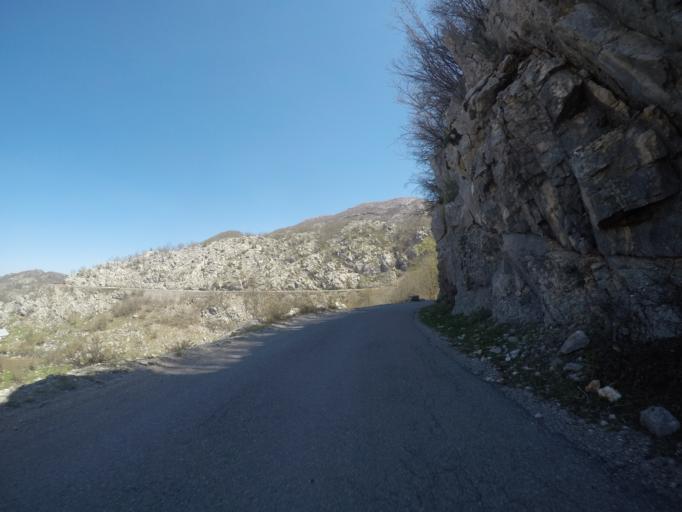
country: ME
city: Dobrota
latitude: 42.4700
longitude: 18.8578
